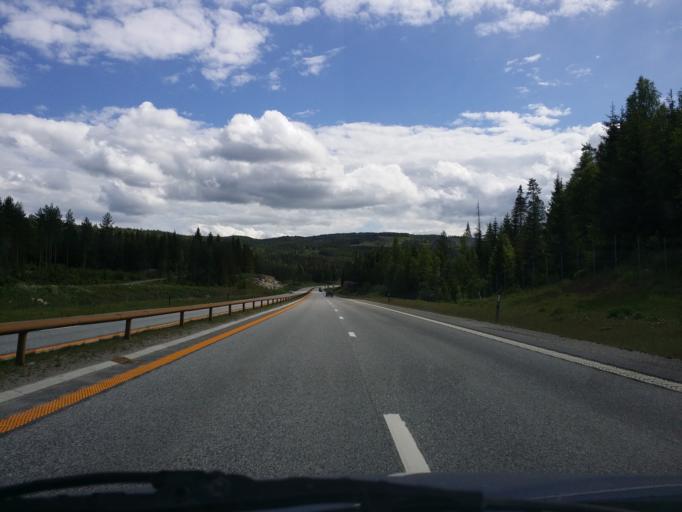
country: NO
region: Hedmark
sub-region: Stange
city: Stange
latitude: 60.6150
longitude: 11.3029
